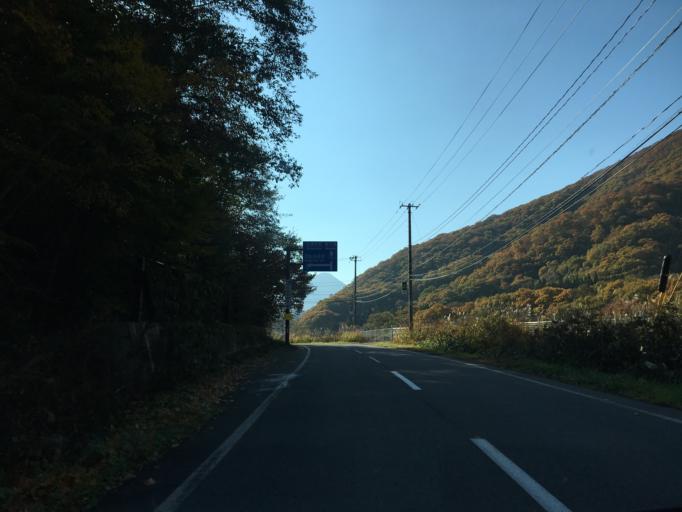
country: JP
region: Fukushima
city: Inawashiro
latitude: 37.2762
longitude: 140.0468
